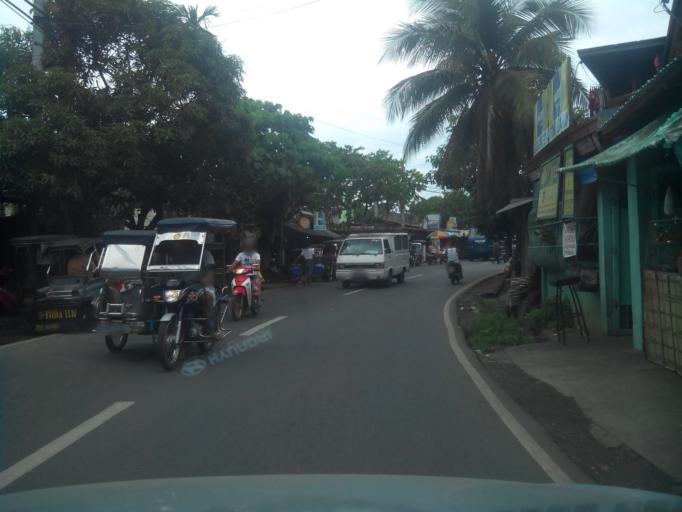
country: PH
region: Calabarzon
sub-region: Province of Rizal
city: Teresa
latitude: 14.5915
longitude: 121.1795
